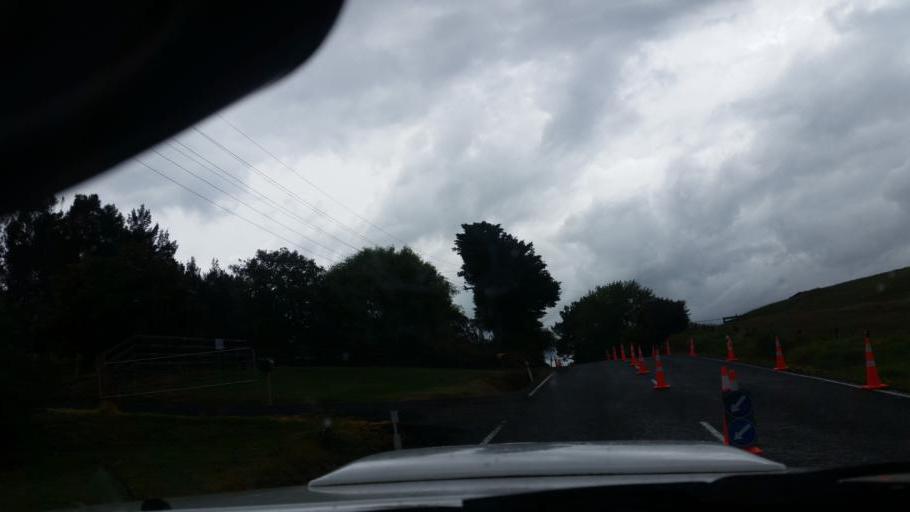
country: NZ
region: Auckland
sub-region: Auckland
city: Wellsford
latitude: -36.1487
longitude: 174.2209
